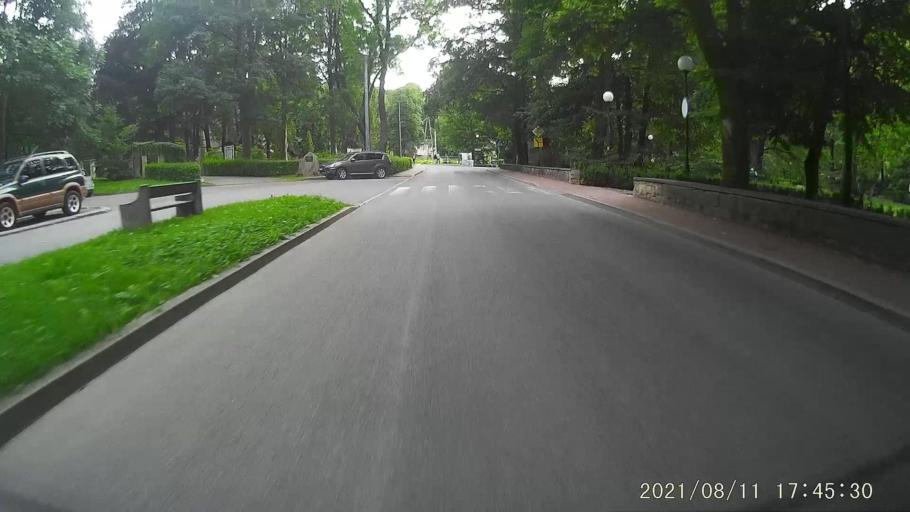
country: PL
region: Lower Silesian Voivodeship
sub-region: Powiat klodzki
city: Duszniki-Zdroj
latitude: 50.3919
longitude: 16.3830
